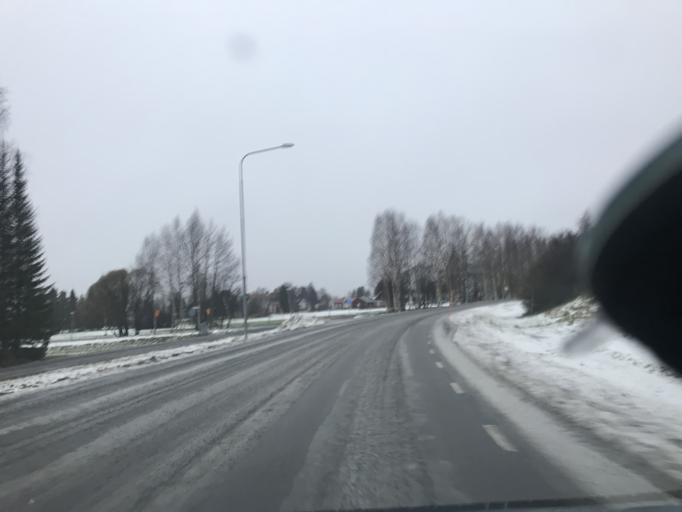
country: SE
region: Norrbotten
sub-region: Lulea Kommun
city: Sodra Sunderbyn
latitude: 65.6550
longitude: 21.9462
